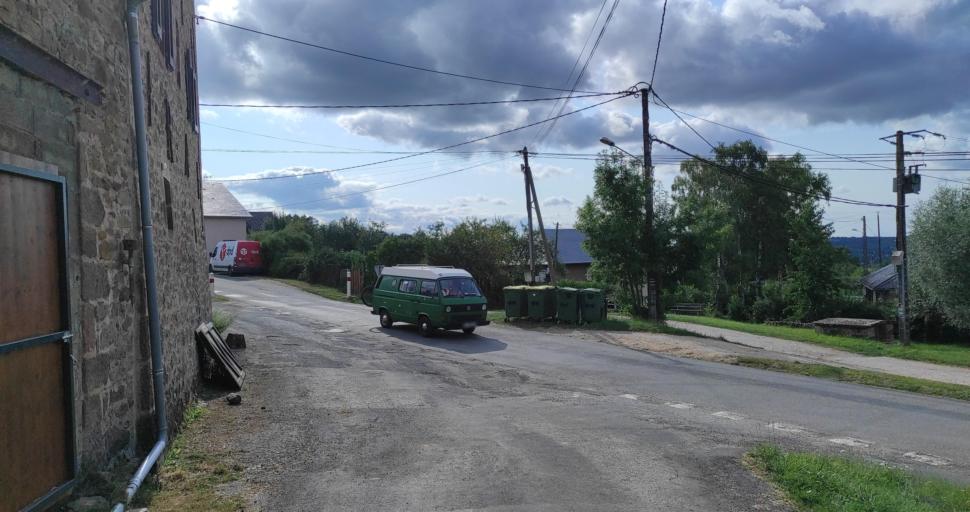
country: FR
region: Midi-Pyrenees
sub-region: Departement de l'Aveyron
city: La Loubiere
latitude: 44.3845
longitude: 2.7104
